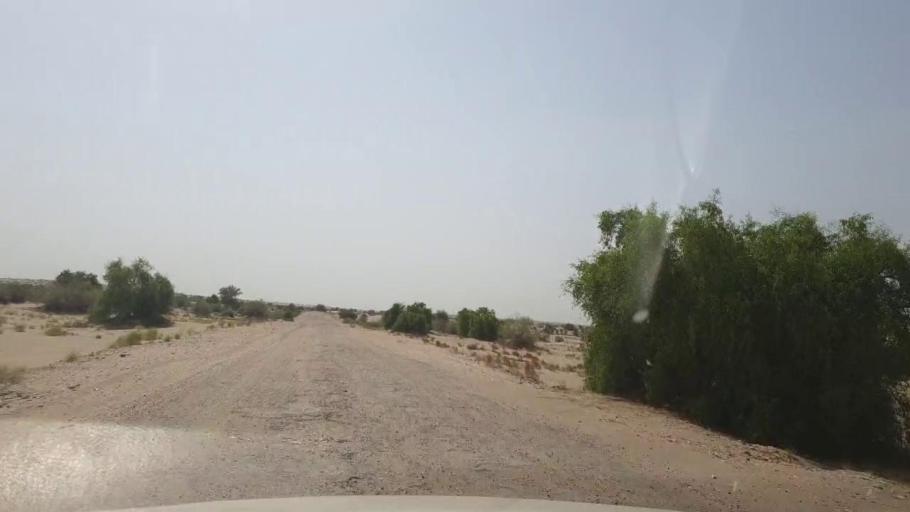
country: PK
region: Sindh
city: Khanpur
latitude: 27.4313
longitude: 69.2535
